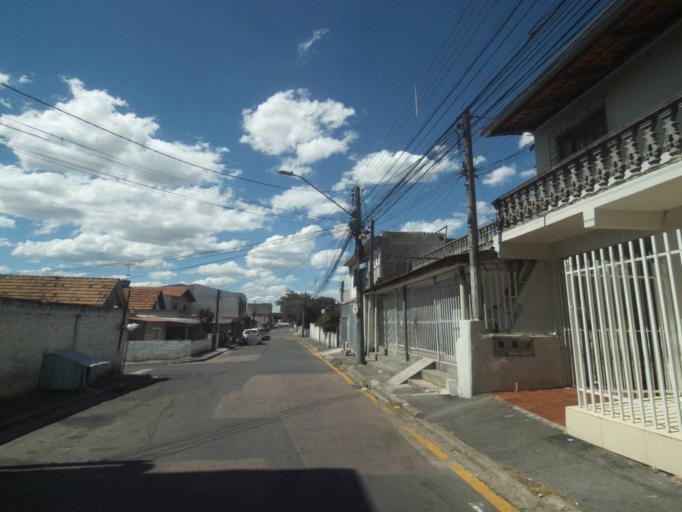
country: BR
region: Parana
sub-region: Curitiba
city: Curitiba
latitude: -25.5031
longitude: -49.3228
